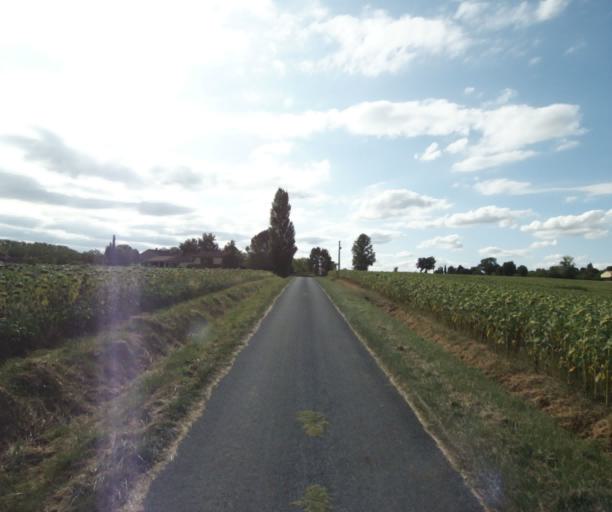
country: FR
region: Midi-Pyrenees
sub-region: Departement du Tarn
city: Puylaurens
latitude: 43.5305
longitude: 1.9942
